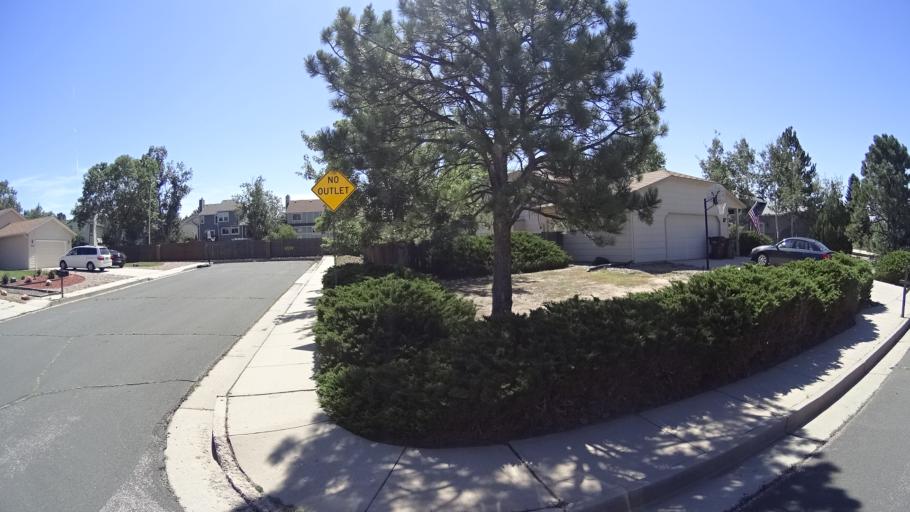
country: US
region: Colorado
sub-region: El Paso County
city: Black Forest
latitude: 38.9448
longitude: -104.7557
